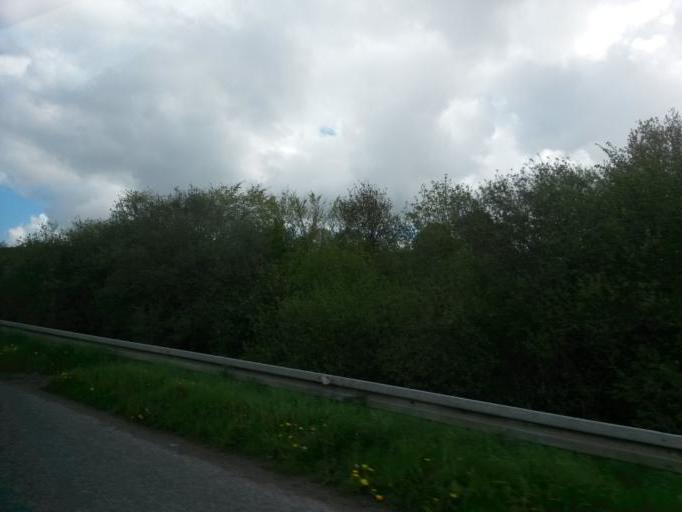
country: IE
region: Leinster
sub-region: Loch Garman
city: Enniscorthy
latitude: 52.4812
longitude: -6.5644
